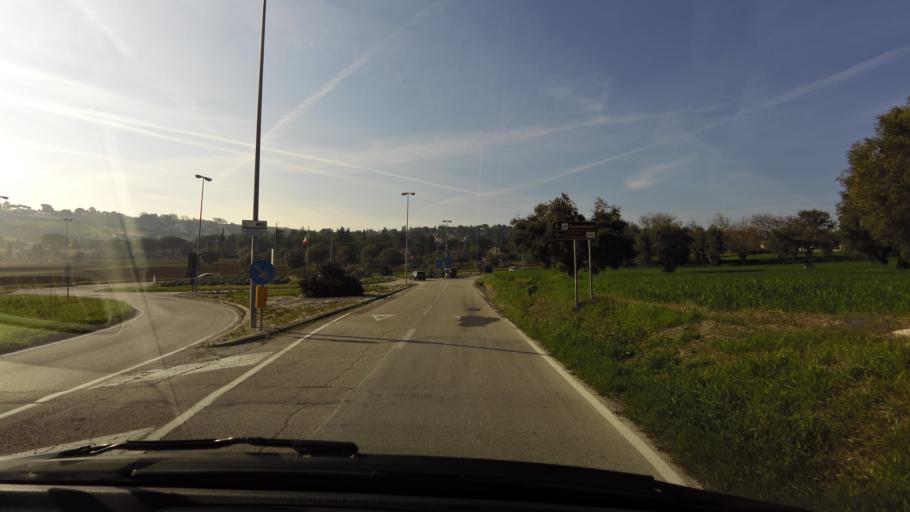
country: IT
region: The Marches
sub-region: Provincia di Ancona
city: Marcelli
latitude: 43.4996
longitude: 13.6177
